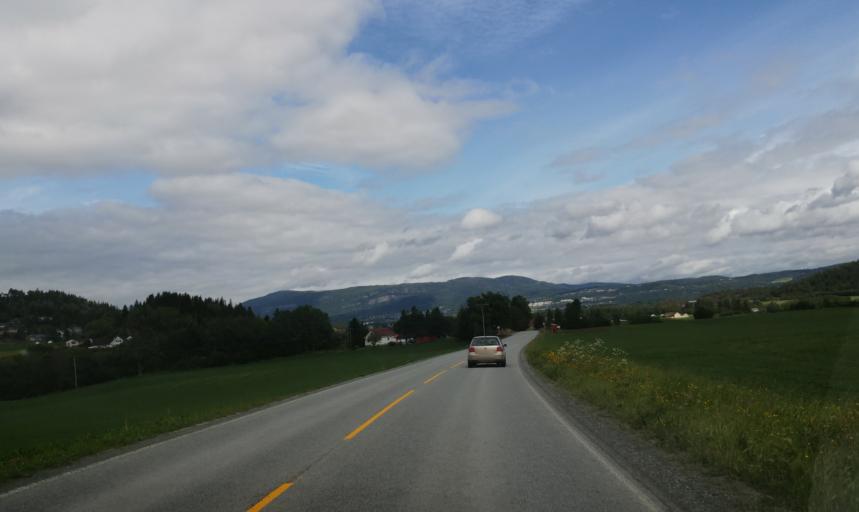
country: NO
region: Nord-Trondelag
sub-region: Stjordal
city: Stjordalshalsen
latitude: 63.4287
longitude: 10.9267
